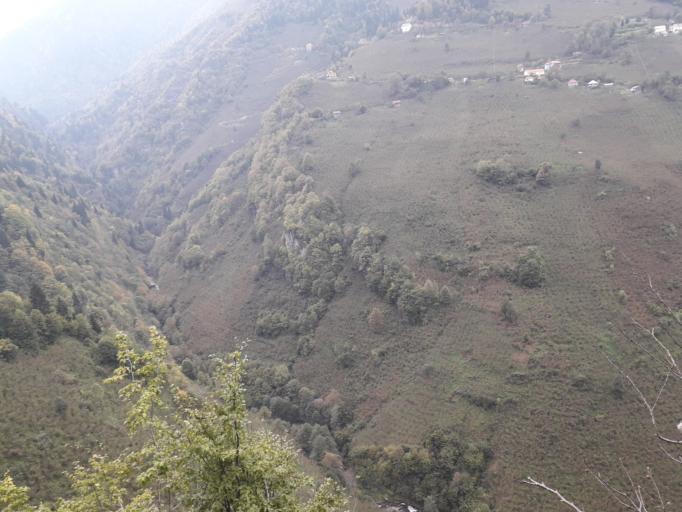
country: TR
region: Ordu
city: Topcam
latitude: 40.7144
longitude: 37.8533
